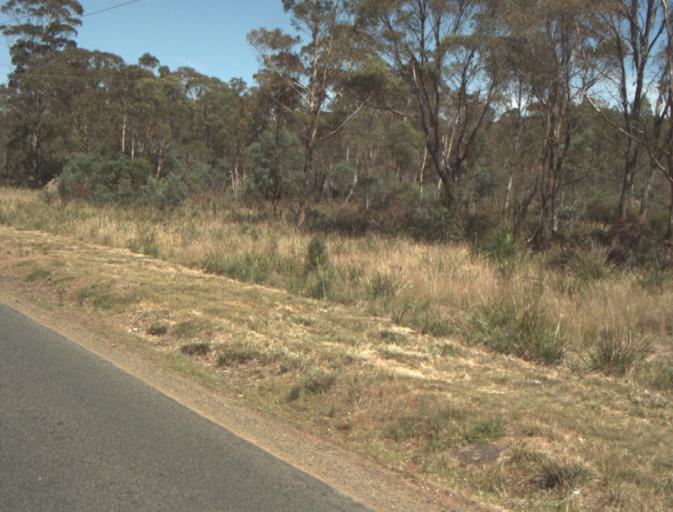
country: AU
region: Tasmania
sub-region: Launceston
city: Mayfield
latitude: -41.3253
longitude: 147.1379
